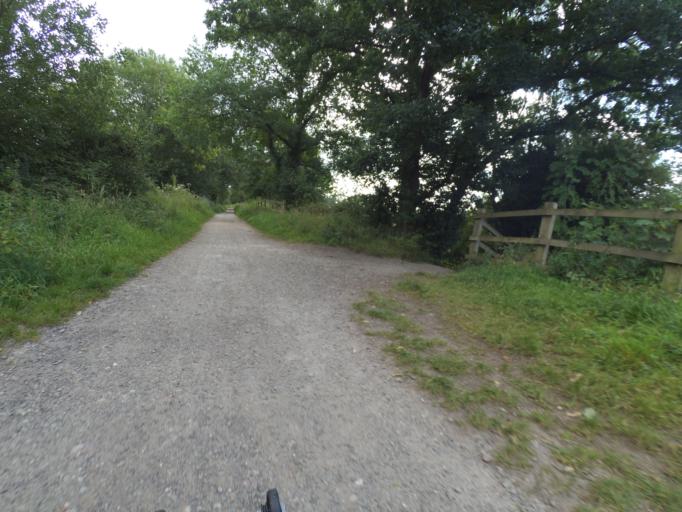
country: GB
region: England
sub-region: Staffordshire
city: Gnosall
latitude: 52.7823
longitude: -2.2707
